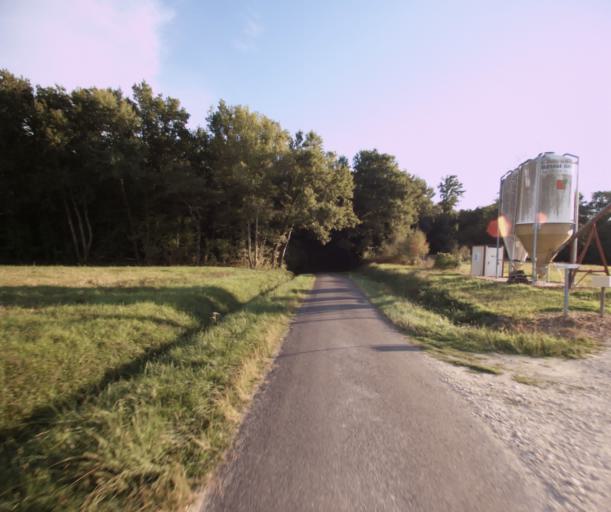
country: FR
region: Midi-Pyrenees
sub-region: Departement du Gers
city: Cazaubon
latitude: 43.8769
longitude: -0.0033
